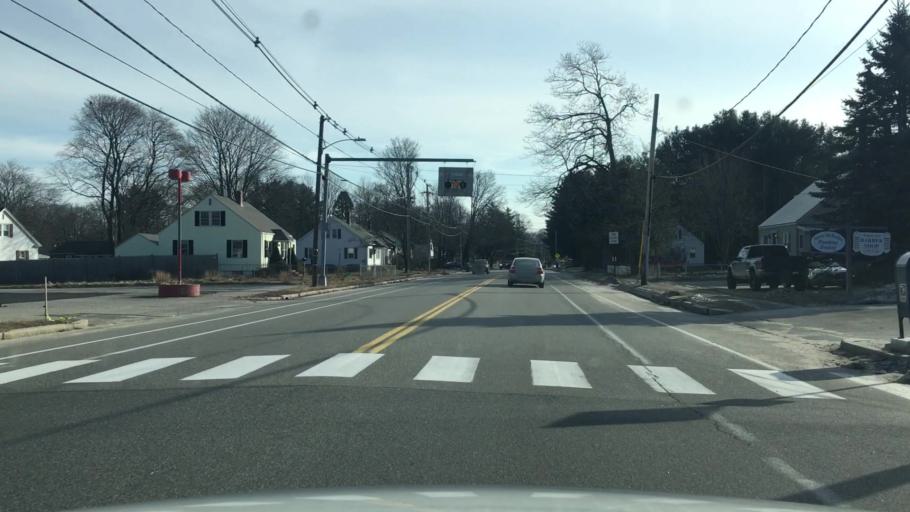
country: US
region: Maine
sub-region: Cumberland County
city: South Portland Gardens
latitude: 43.6966
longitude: -70.3063
